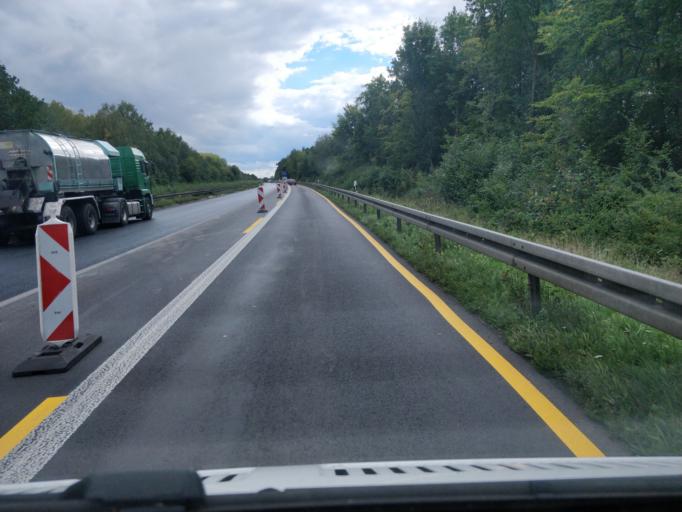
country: DE
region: North Rhine-Westphalia
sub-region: Regierungsbezirk Koln
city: Frechen
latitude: 50.8735
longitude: 6.8019
